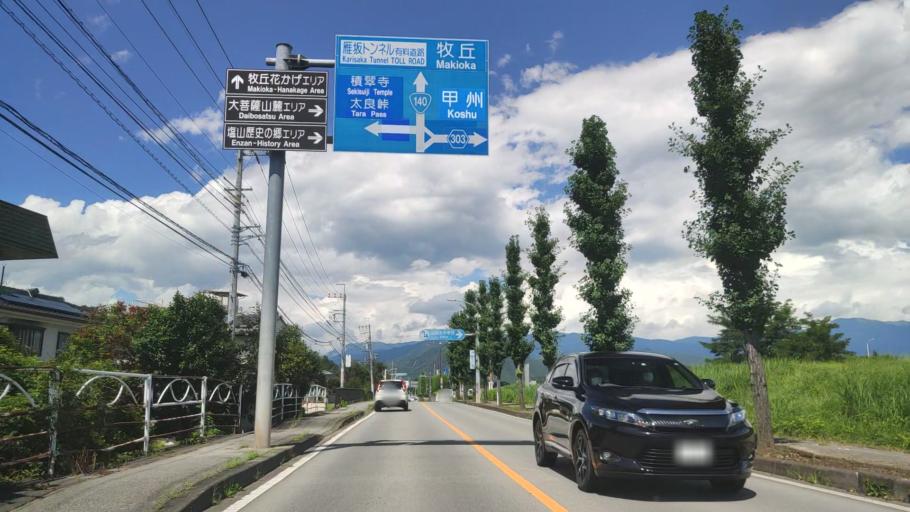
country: JP
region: Yamanashi
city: Enzan
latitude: 35.7023
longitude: 138.6917
